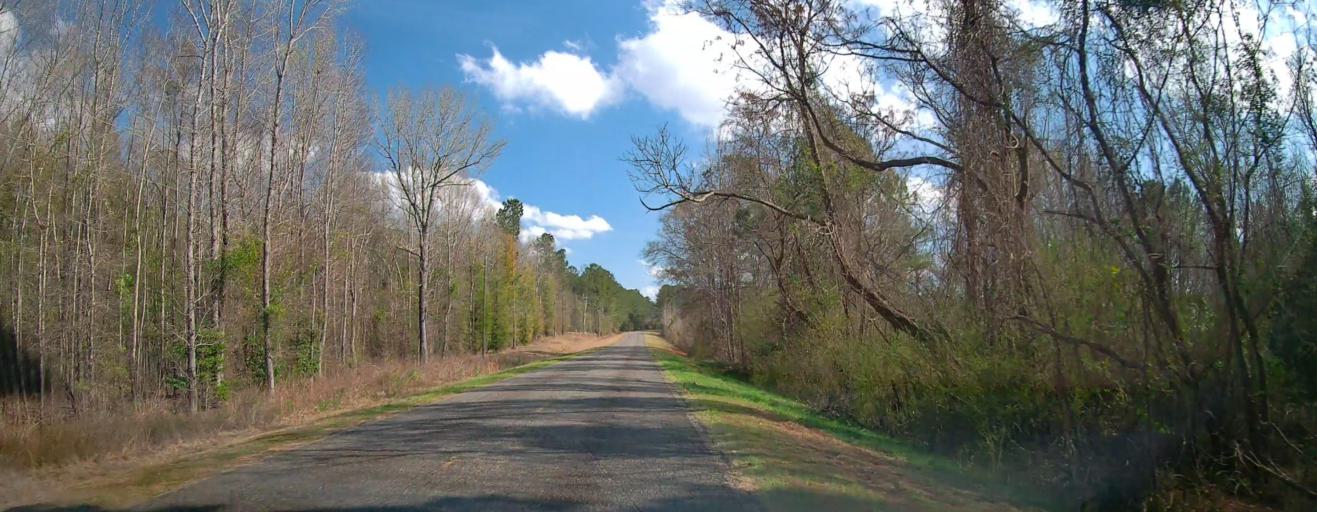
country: US
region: Georgia
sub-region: Twiggs County
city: Jeffersonville
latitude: 32.6740
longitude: -83.2389
